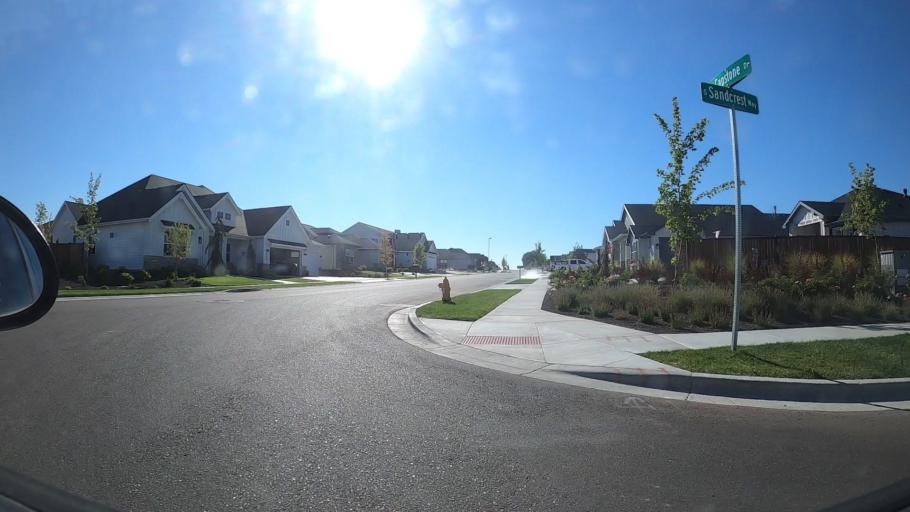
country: US
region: Idaho
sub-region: Canyon County
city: Nampa
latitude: 43.5471
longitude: -116.5987
